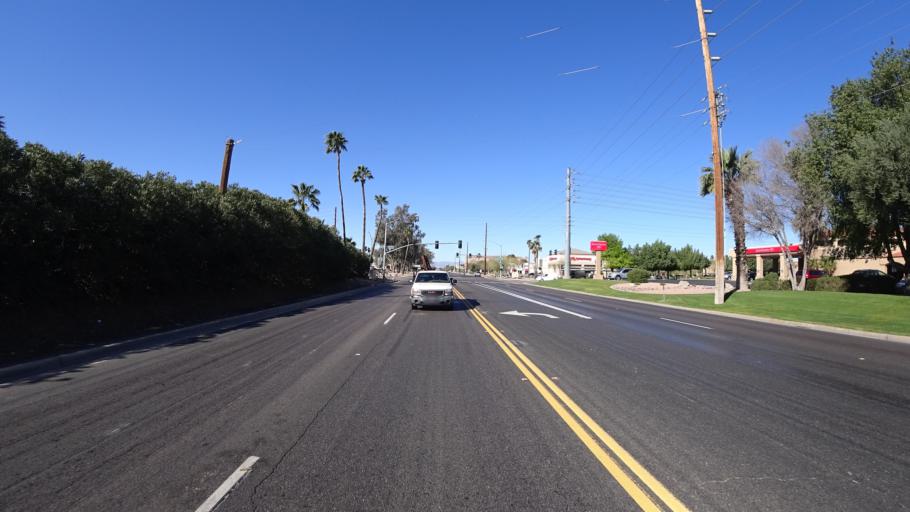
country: US
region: Arizona
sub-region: Maricopa County
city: Sun Lakes
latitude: 33.2180
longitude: -111.8752
